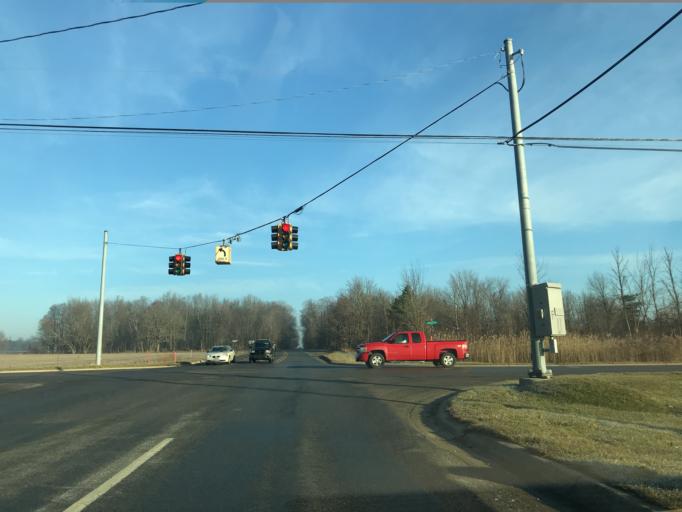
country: US
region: Michigan
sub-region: Eaton County
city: Dimondale
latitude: 42.6400
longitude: -84.6029
